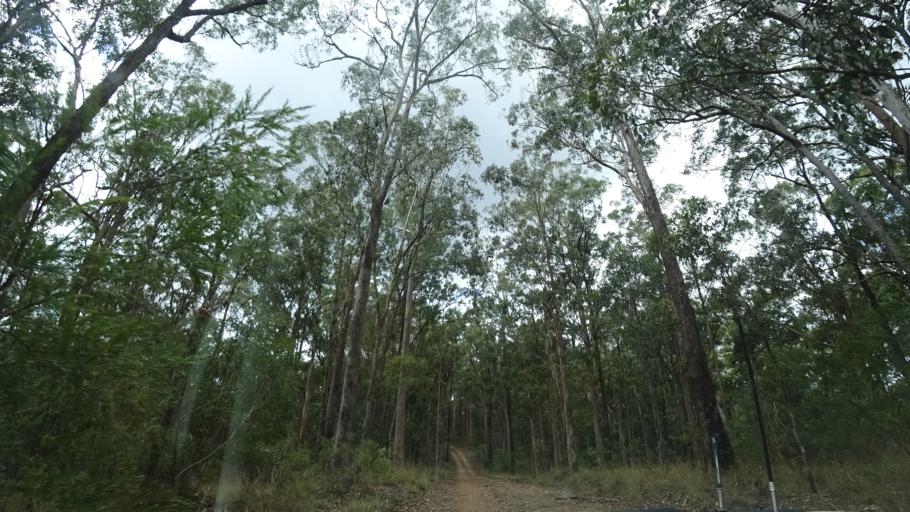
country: AU
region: Queensland
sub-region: Moreton Bay
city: Highvale
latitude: -27.3899
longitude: 152.7459
